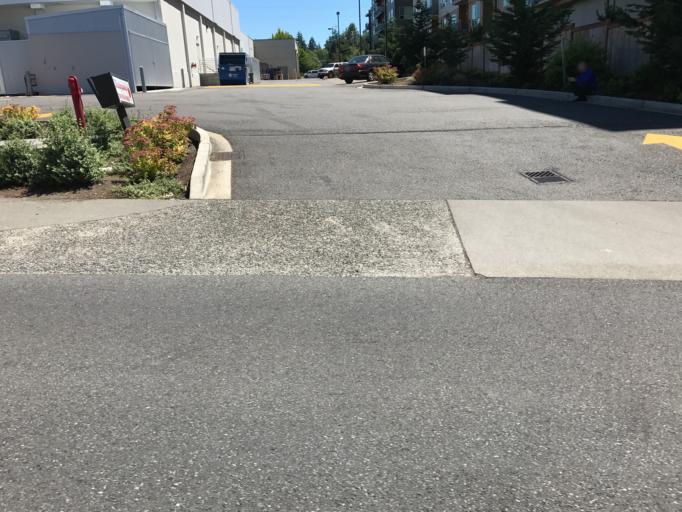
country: US
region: Washington
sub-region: King County
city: Redmond
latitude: 47.6303
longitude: -122.1344
